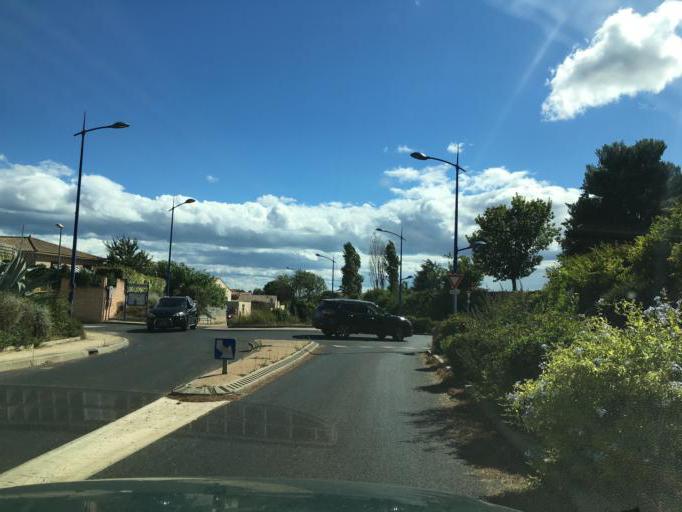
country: FR
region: Languedoc-Roussillon
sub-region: Departement de l'Herault
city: Pomerols
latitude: 43.3959
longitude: 3.5024
